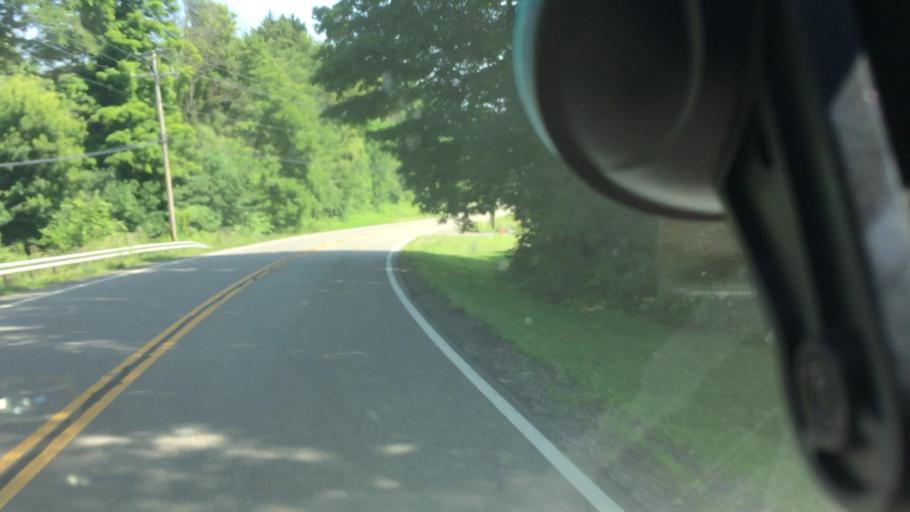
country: US
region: Ohio
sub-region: Columbiana County
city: Lisbon
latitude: 40.7586
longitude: -80.7865
